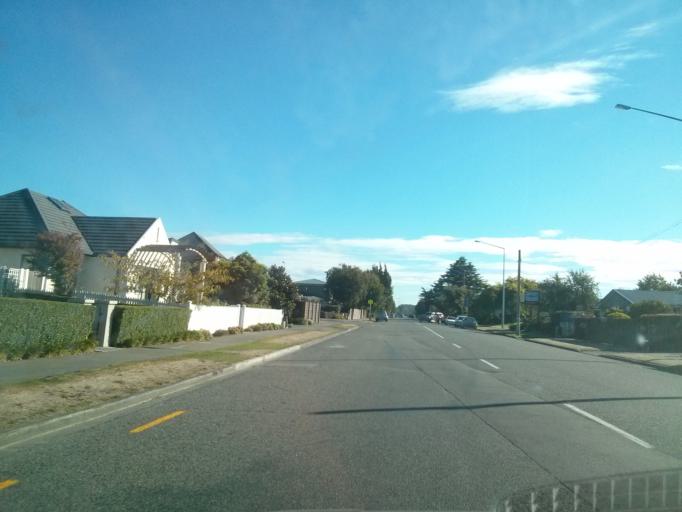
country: NZ
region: Canterbury
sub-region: Christchurch City
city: Christchurch
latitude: -43.4972
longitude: 172.5631
